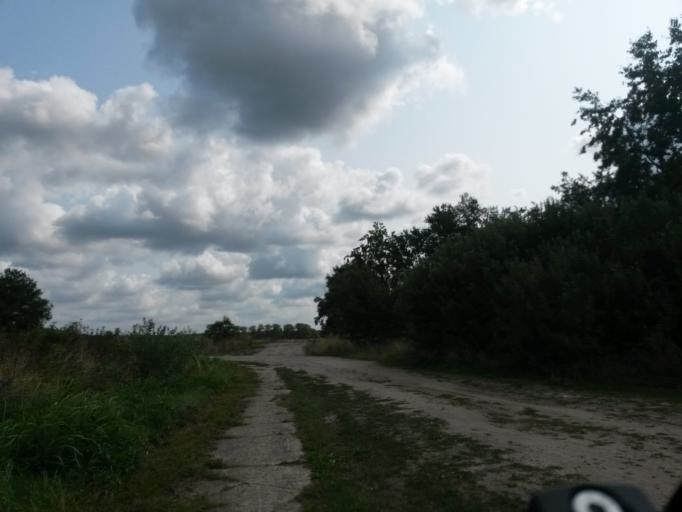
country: DE
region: Saxony-Anhalt
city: Klietz
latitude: 52.6570
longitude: 12.0495
